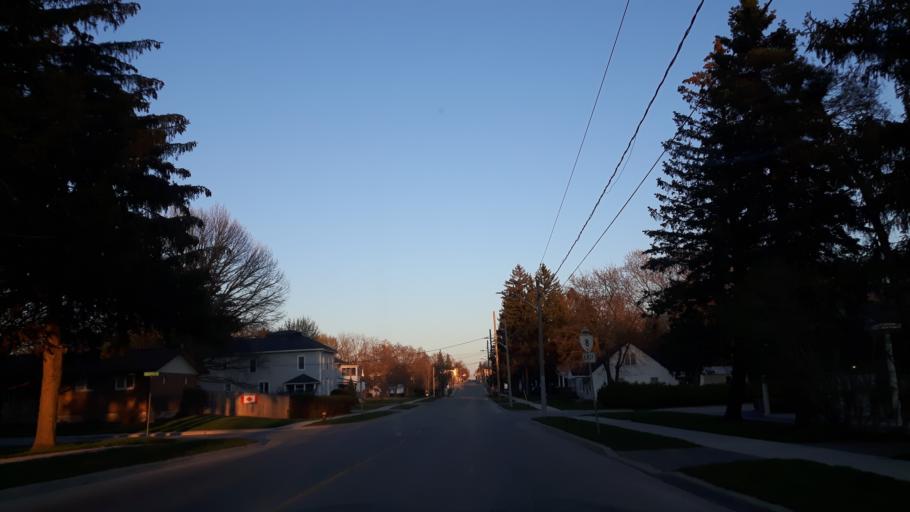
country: CA
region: Ontario
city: Bluewater
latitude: 43.6197
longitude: -81.5457
